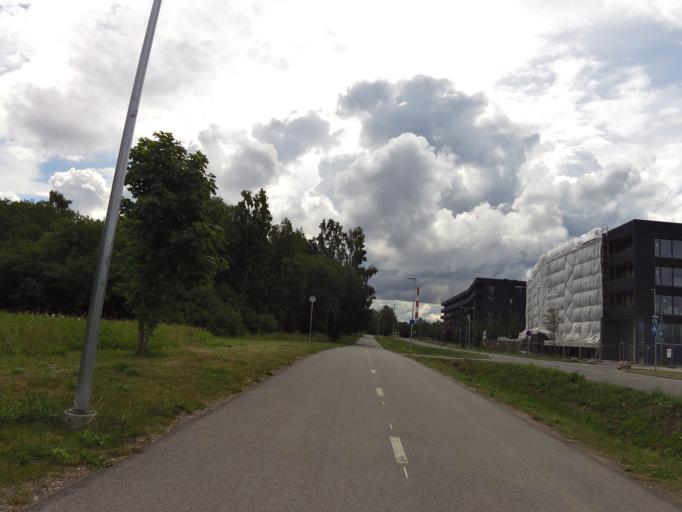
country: EE
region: Harju
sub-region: Tallinna linn
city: Tallinn
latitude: 59.4334
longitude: 24.6853
